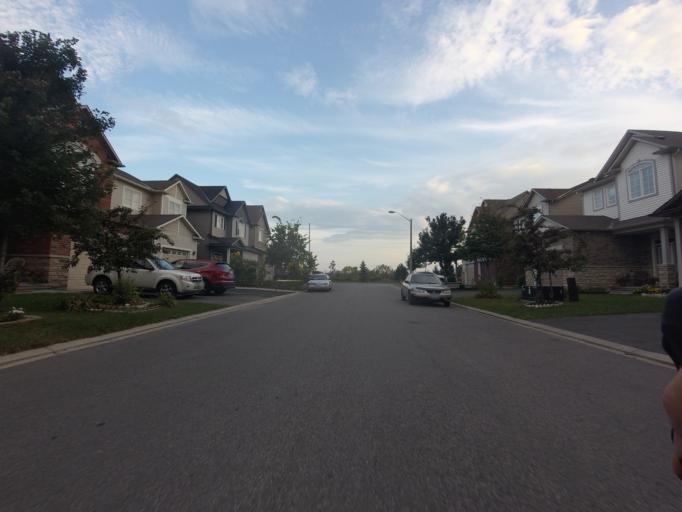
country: CA
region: Ontario
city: Bells Corners
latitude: 45.2616
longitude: -75.7628
